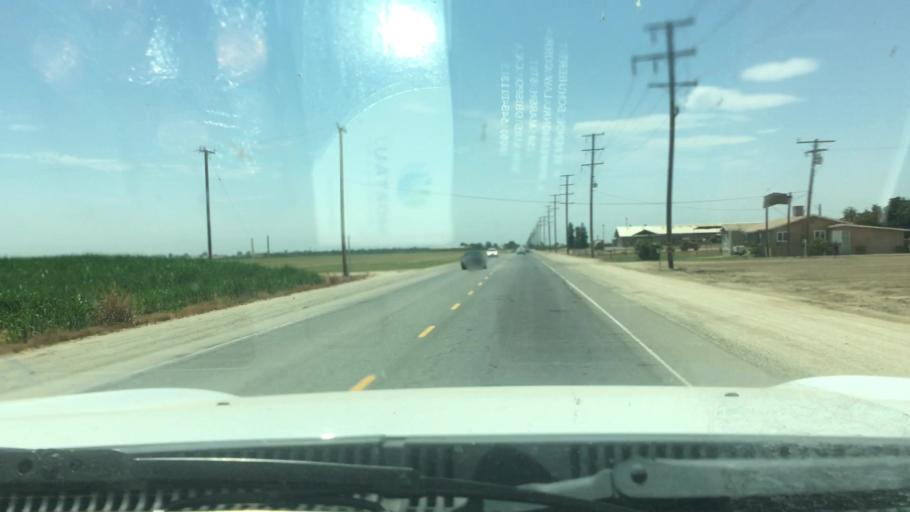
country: US
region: California
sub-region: Tulare County
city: Tipton
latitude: 36.0657
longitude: -119.2673
